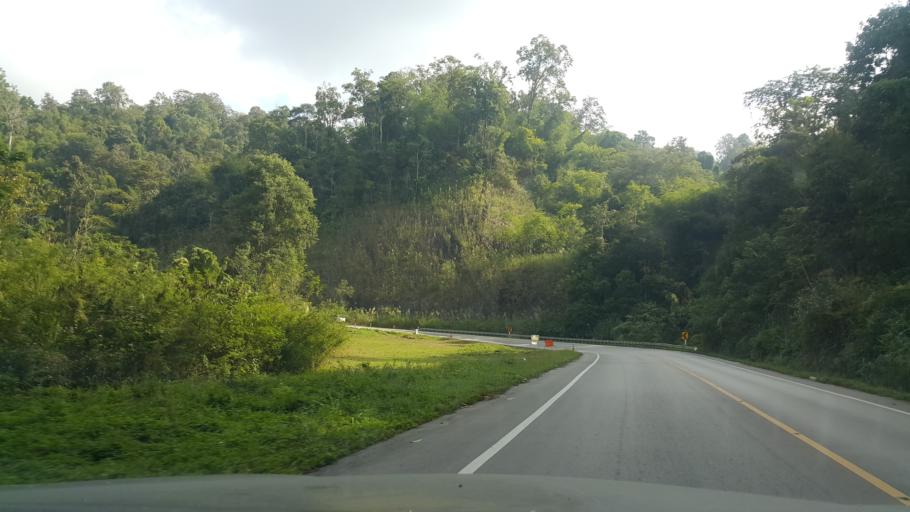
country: TH
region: Lampang
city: Wang Nuea
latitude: 19.0644
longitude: 99.7285
